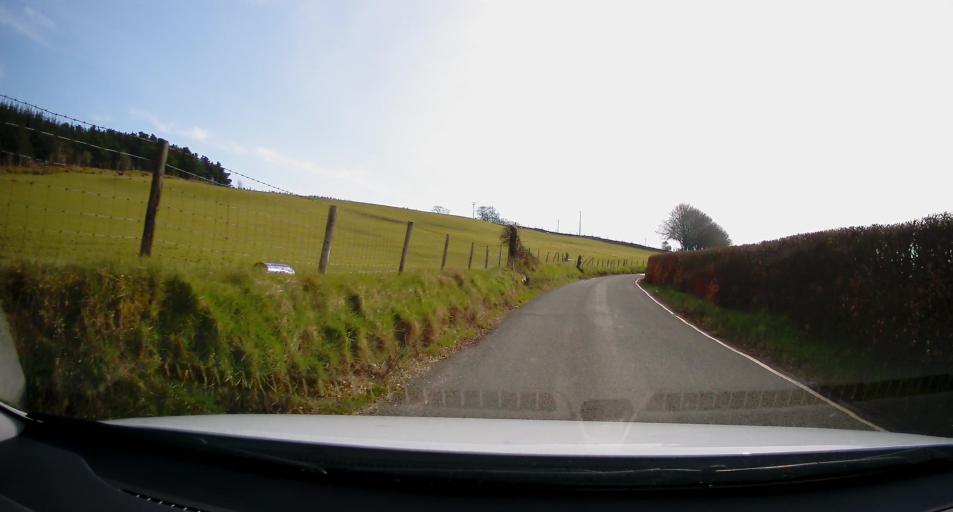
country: GB
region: Wales
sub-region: County of Ceredigion
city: Lledrod
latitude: 52.2599
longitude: -4.0749
